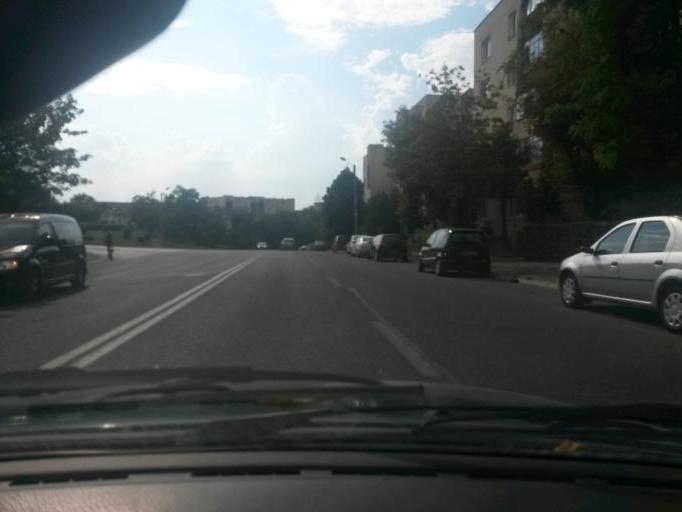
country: RO
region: Mures
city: Targu-Mures
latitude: 46.5336
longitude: 24.5686
